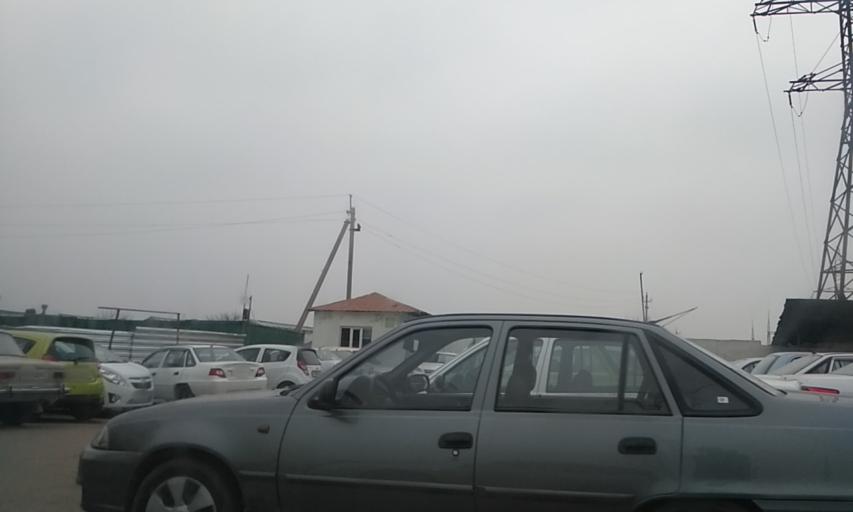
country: UZ
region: Toshkent Shahri
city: Tashkent
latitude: 41.2897
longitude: 69.1501
